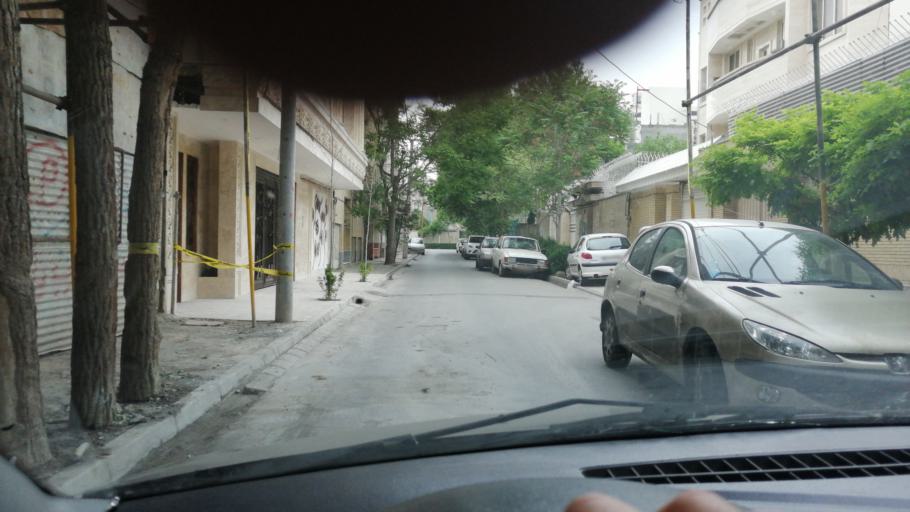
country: IR
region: Razavi Khorasan
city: Mashhad
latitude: 36.2874
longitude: 59.5862
